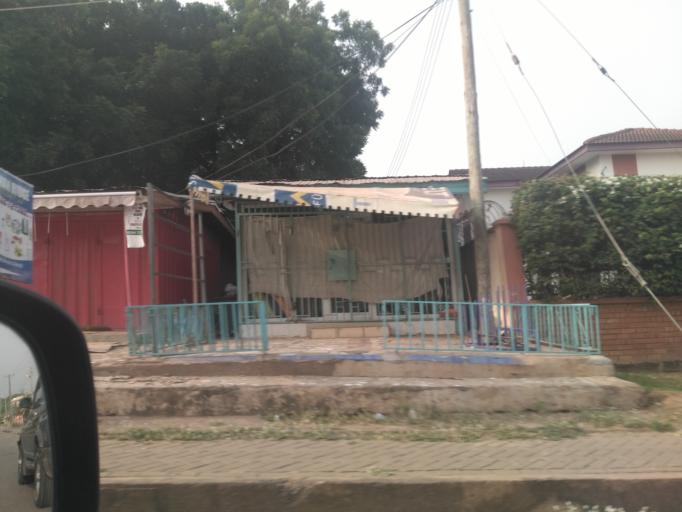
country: GH
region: Greater Accra
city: Accra
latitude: 5.6050
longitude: -0.1953
